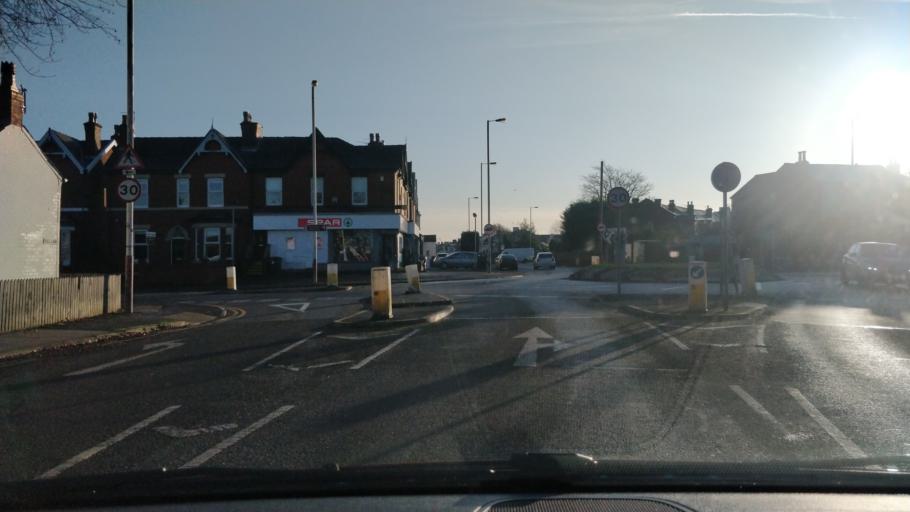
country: GB
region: England
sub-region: Sefton
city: Southport
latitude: 53.6546
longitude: -2.9653
